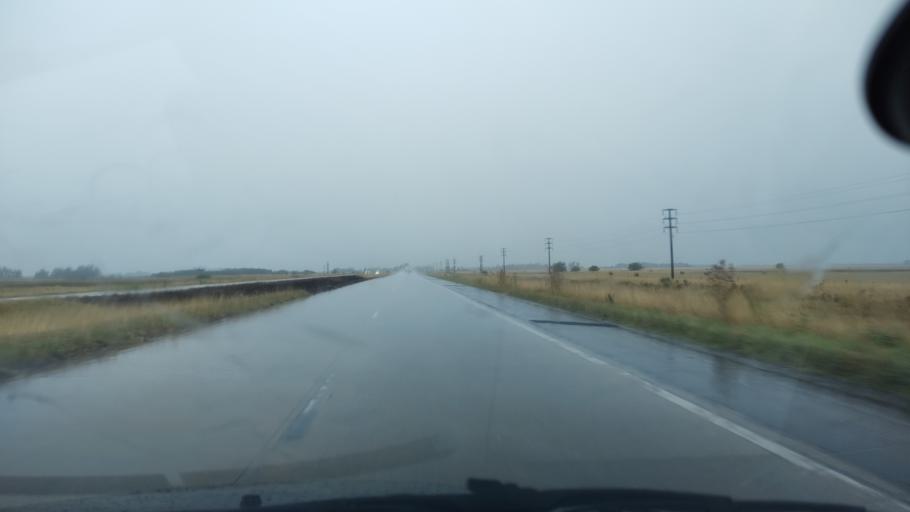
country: AR
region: Buenos Aires
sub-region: Partido de San Vicente
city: San Vicente
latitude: -35.0731
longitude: -58.5382
